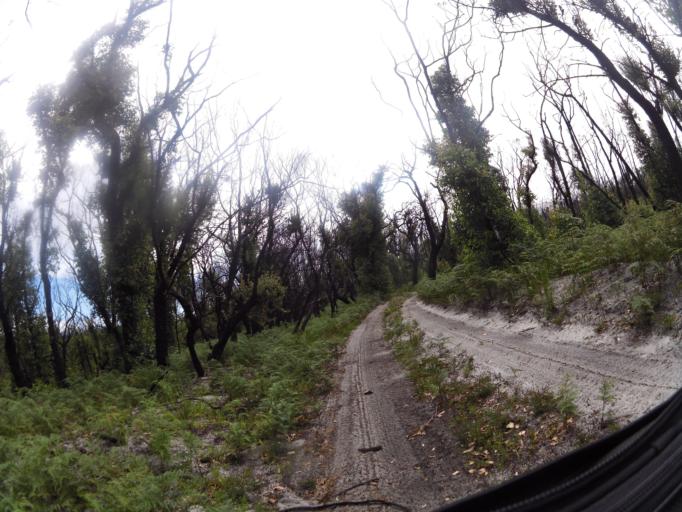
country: AU
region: Victoria
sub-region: East Gippsland
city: Lakes Entrance
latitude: -37.8016
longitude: 148.7370
